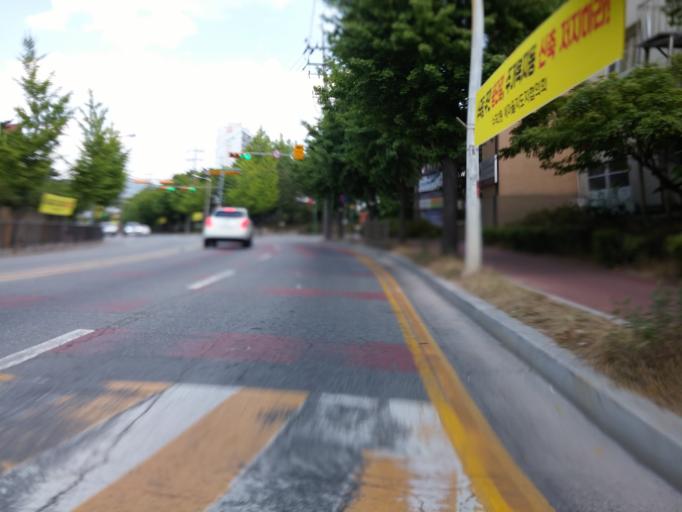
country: KR
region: Chungcheongbuk-do
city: Cheongju-si
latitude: 36.6177
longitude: 127.4762
